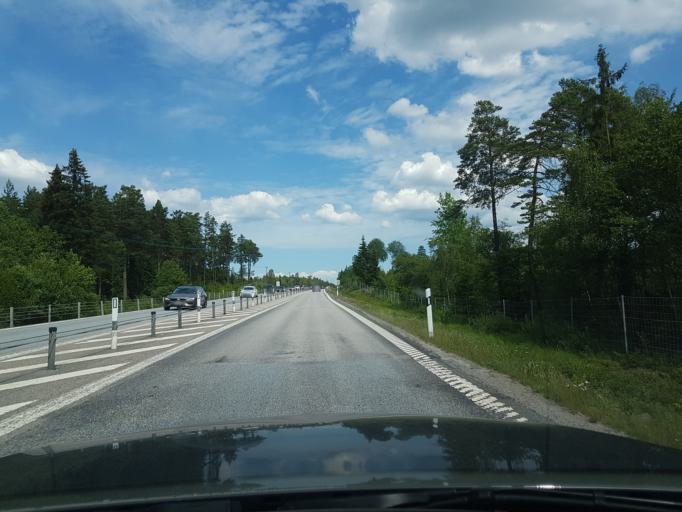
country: SE
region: Stockholm
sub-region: Osterakers Kommun
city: Akersberga
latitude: 59.5786
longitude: 18.2432
